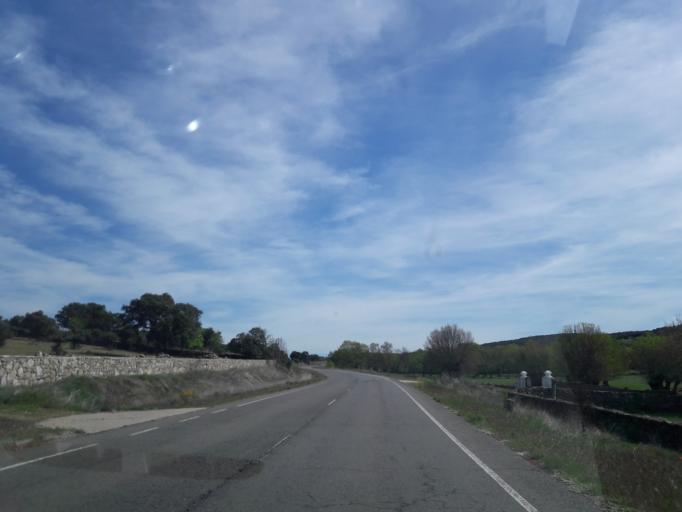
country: ES
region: Castille and Leon
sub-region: Provincia de Salamanca
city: Ledrada
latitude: 40.4922
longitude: -5.7173
